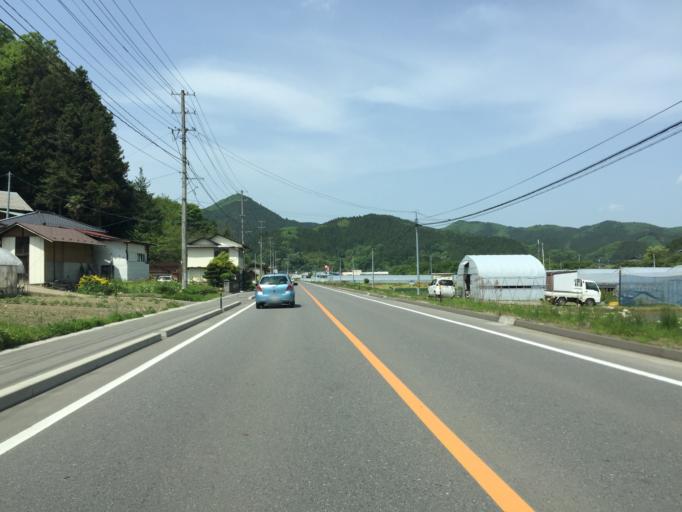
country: JP
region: Fukushima
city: Ishikawa
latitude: 37.0880
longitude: 140.5273
